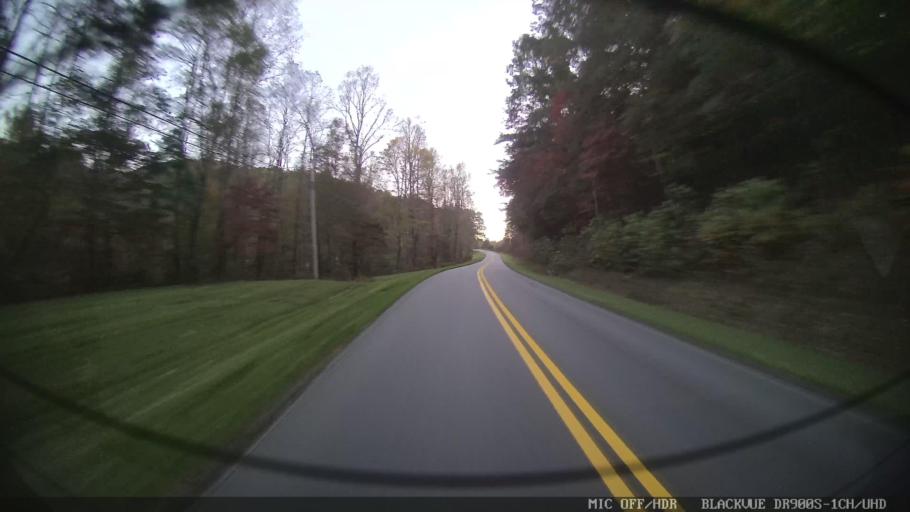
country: US
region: Georgia
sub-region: Union County
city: Blairsville
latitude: 34.8992
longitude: -83.8669
